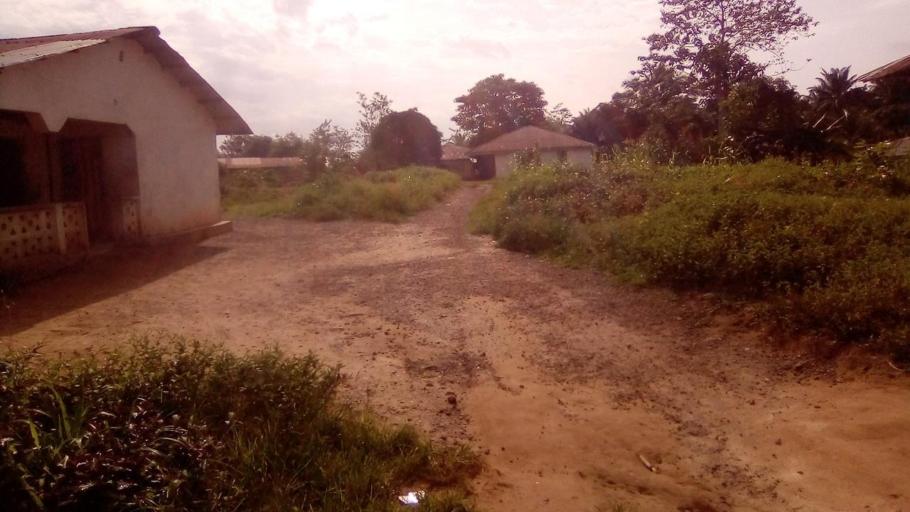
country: SL
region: Southern Province
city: Pujehun
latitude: 7.3640
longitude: -11.7223
